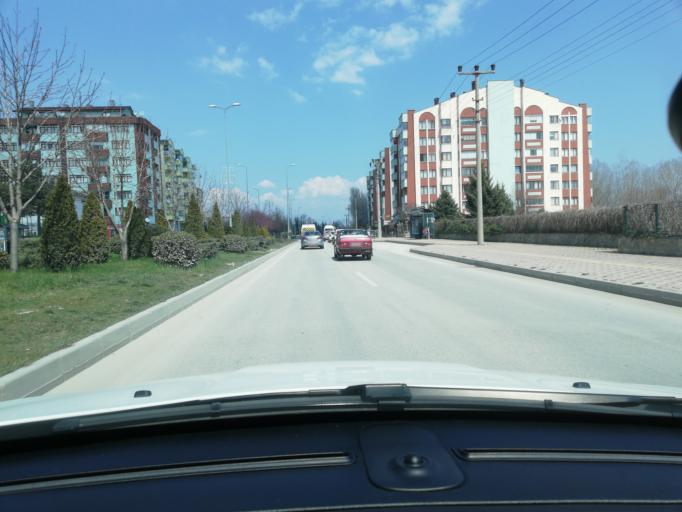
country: TR
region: Kastamonu
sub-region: Cide
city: Kastamonu
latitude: 41.4055
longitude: 33.7852
